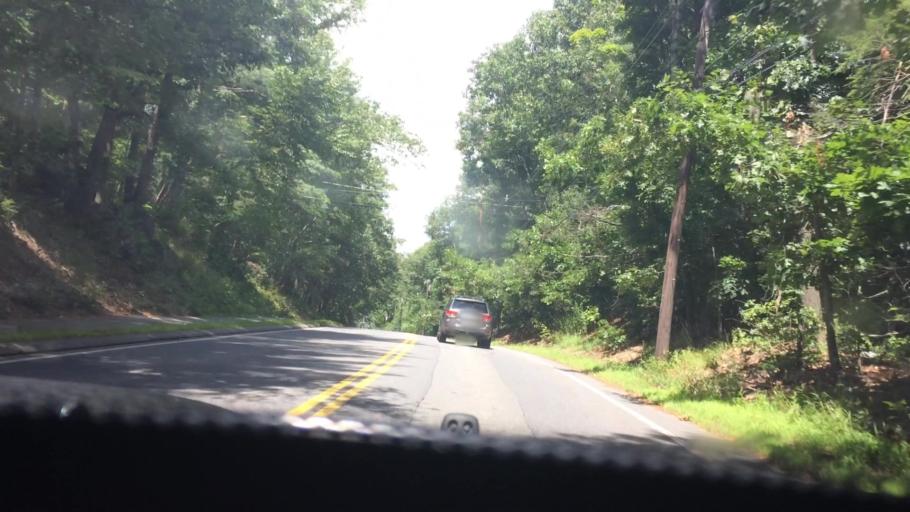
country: US
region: Massachusetts
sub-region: Middlesex County
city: Sudbury
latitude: 42.3947
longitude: -71.4259
